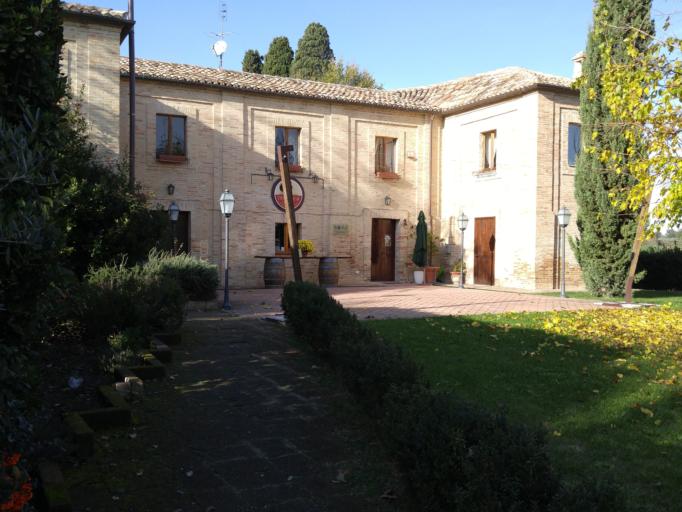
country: IT
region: The Marches
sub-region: Provincia di Pesaro e Urbino
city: Saltara
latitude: 43.7559
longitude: 12.8911
